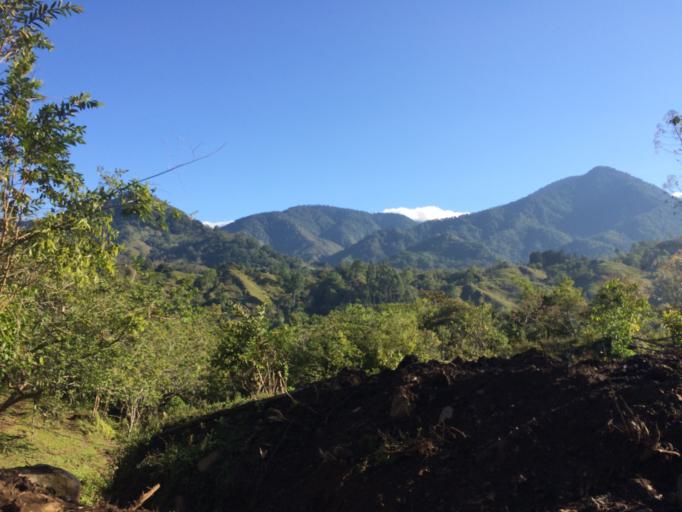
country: CR
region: San Jose
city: San Isidro
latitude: 9.4554
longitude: -83.5973
